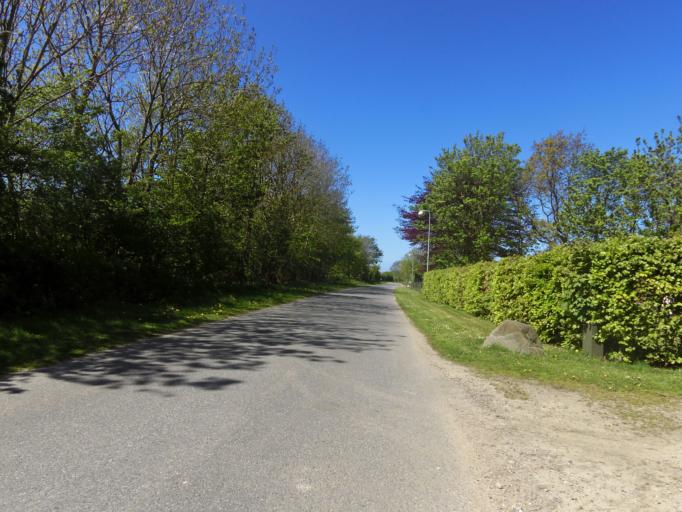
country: DK
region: South Denmark
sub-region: Tonder Kommune
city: Sherrebek
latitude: 55.2348
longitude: 8.7143
